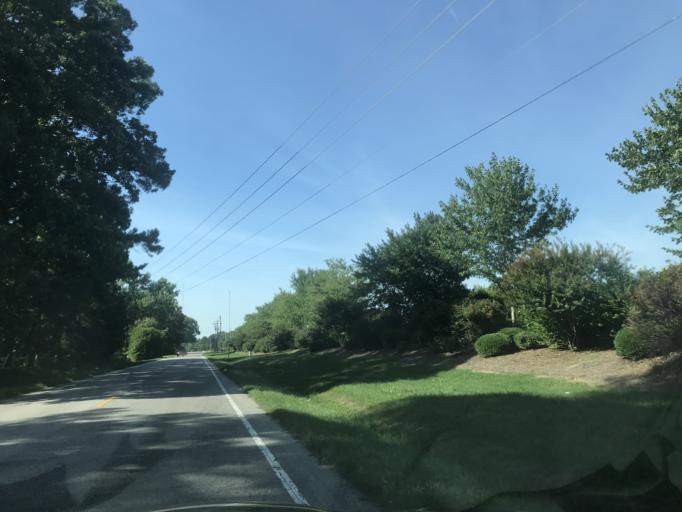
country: US
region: North Carolina
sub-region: Johnston County
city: Clayton
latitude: 35.6259
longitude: -78.5366
